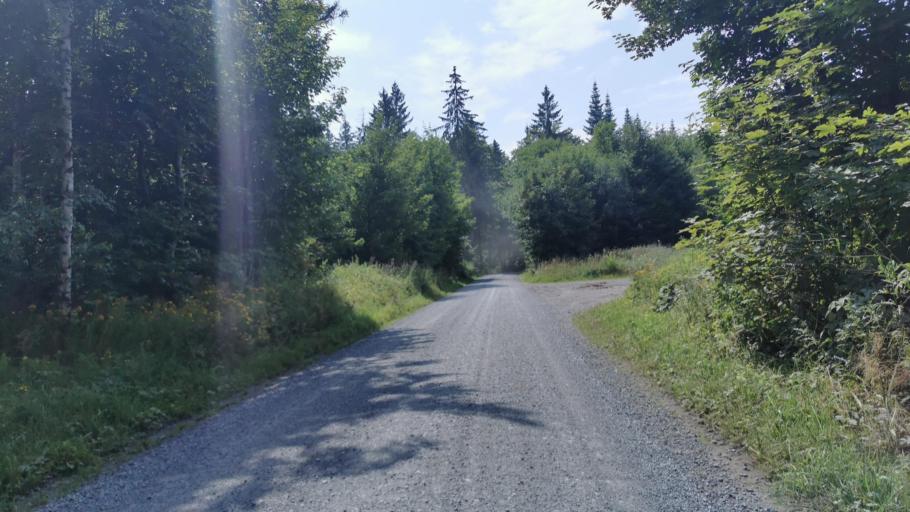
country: DE
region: Bavaria
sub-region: Upper Franconia
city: Wilhelmsthal
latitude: 50.2945
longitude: 11.3993
